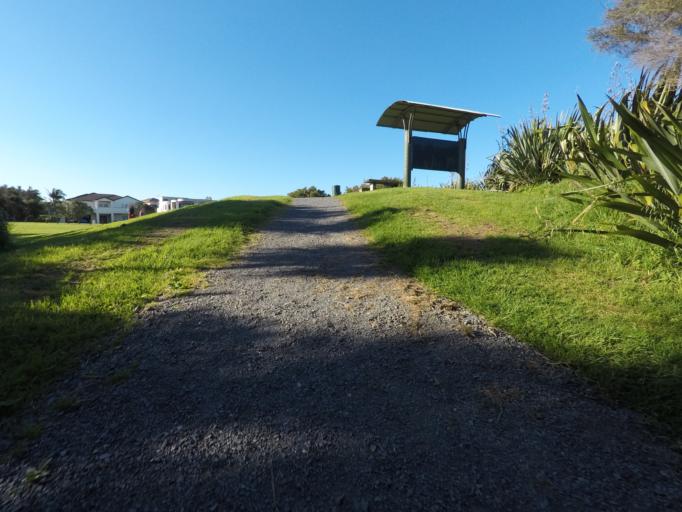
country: NZ
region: Auckland
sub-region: Auckland
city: Rosebank
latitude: -36.8484
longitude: 174.6539
